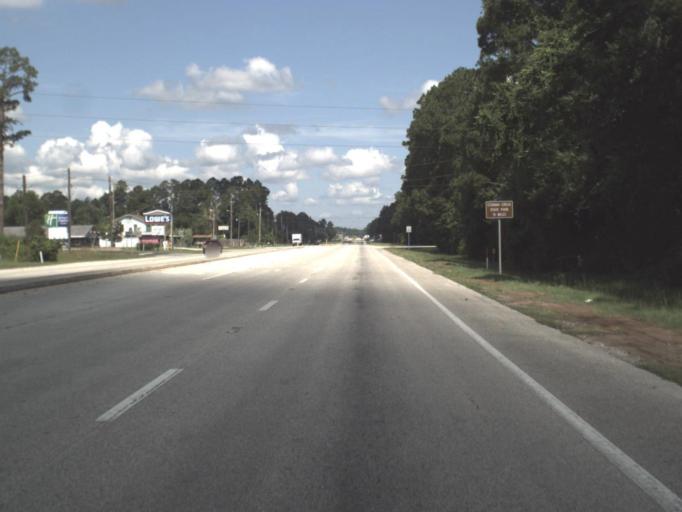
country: US
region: Florida
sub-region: Putnam County
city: Palatka
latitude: 29.6587
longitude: -81.6697
